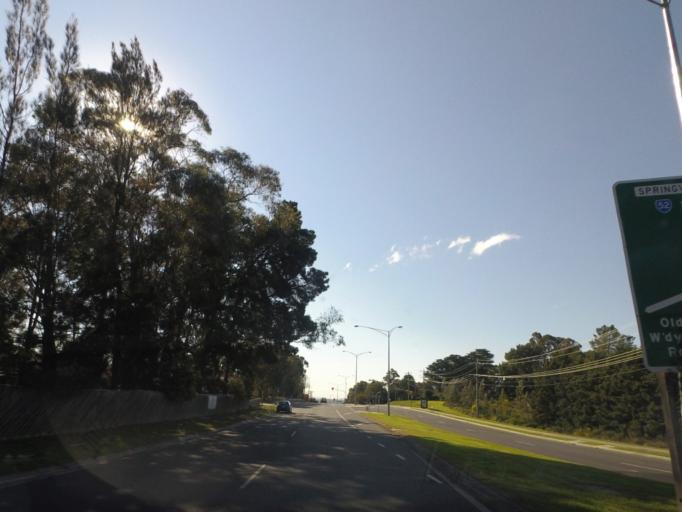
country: AU
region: Victoria
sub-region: Manningham
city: Donvale
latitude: -37.7854
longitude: 145.1813
